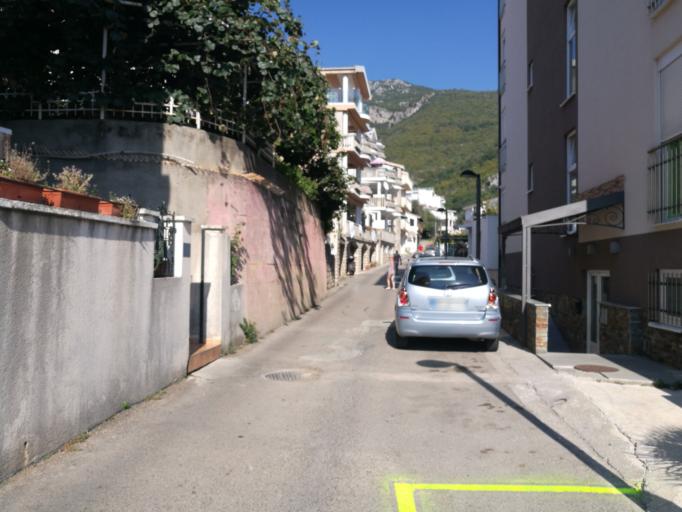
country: ME
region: Budva
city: Budva
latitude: 42.2829
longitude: 18.8812
